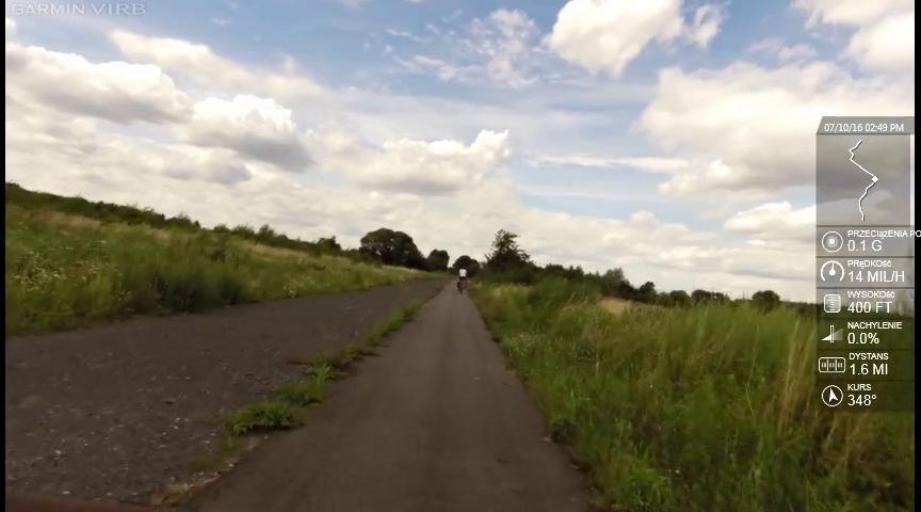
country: PL
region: West Pomeranian Voivodeship
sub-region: Powiat gryfinski
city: Banie
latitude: 53.0979
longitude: 14.6499
